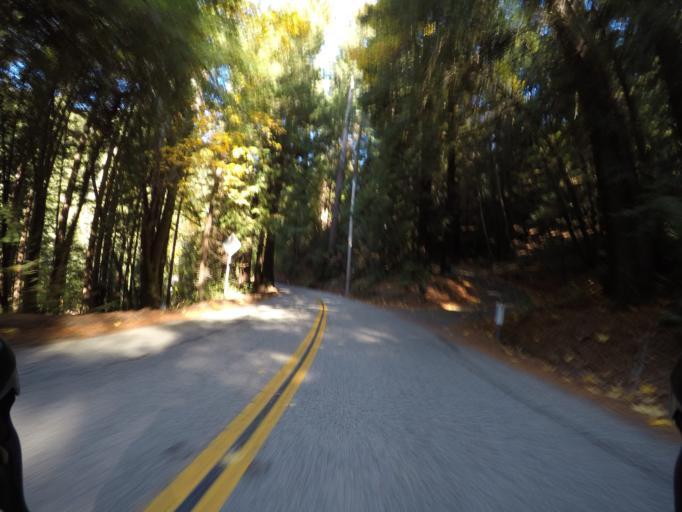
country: US
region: California
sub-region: Santa Cruz County
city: Scotts Valley
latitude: 37.0918
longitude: -122.0049
